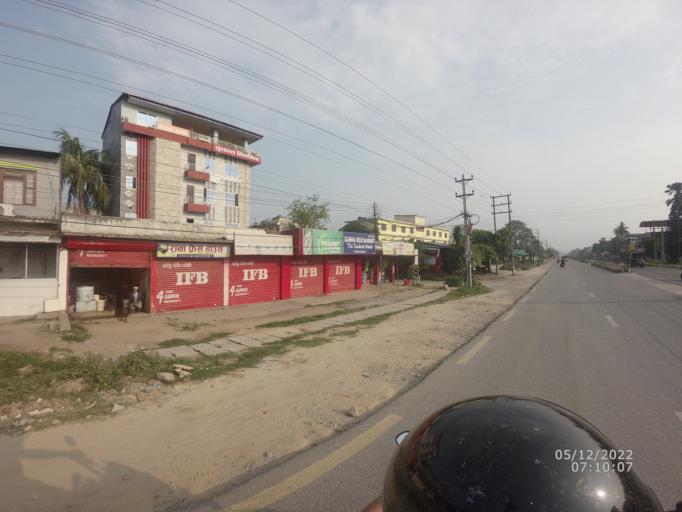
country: NP
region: Central Region
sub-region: Narayani Zone
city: Bharatpur
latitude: 27.6731
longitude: 84.4387
